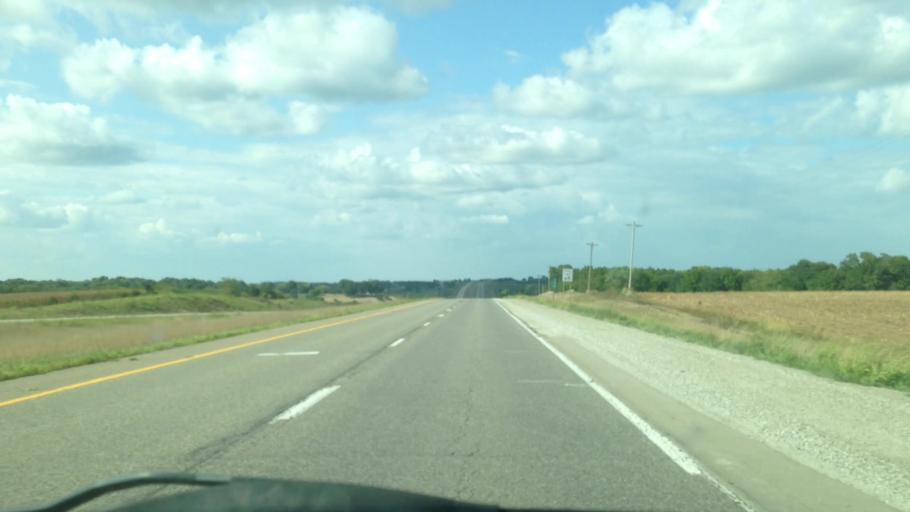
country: US
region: Iowa
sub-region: Henry County
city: Mount Pleasant
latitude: 40.8495
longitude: -91.5646
